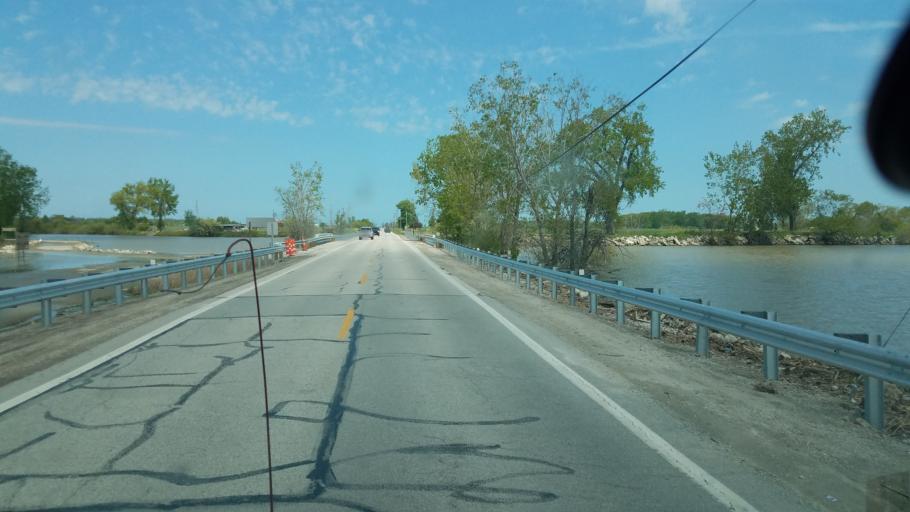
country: US
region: Ohio
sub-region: Ottawa County
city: Oak Harbor
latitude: 41.5789
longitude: -83.1449
